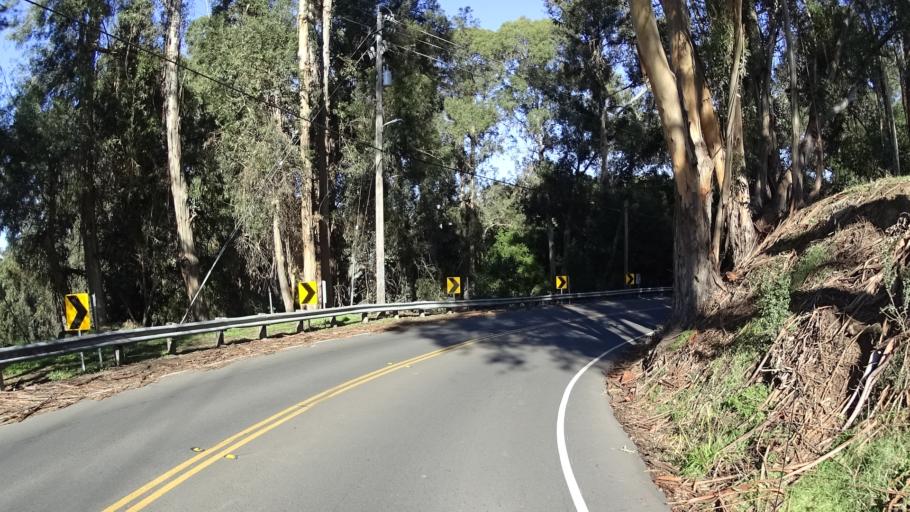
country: US
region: California
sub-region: Alameda County
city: Fairview
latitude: 37.6734
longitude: -122.0557
